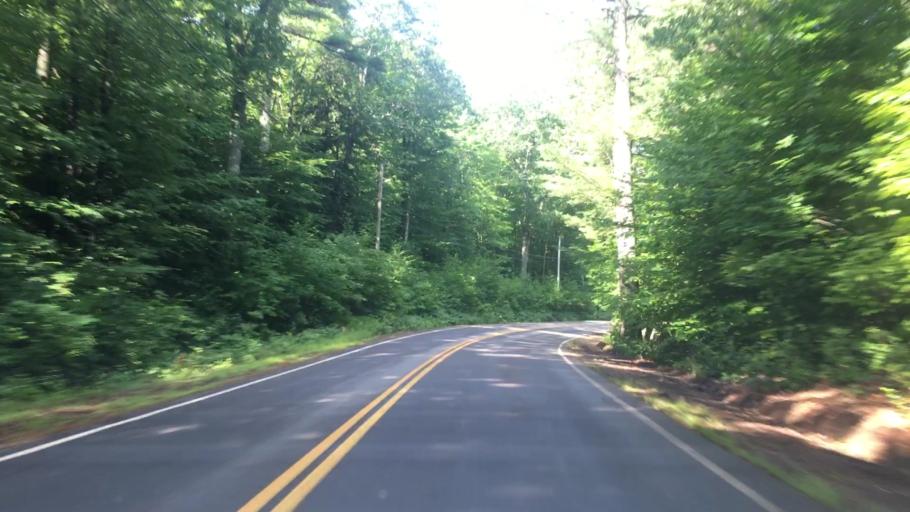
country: US
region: New Hampshire
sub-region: Belknap County
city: Gilford
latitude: 43.5394
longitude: -71.3057
